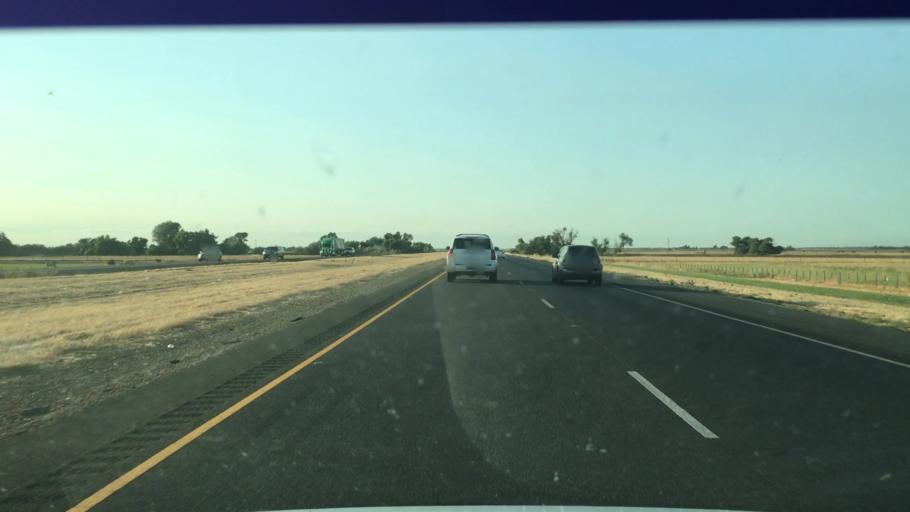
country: US
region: California
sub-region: Sacramento County
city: Laguna
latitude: 38.3406
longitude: -121.4695
